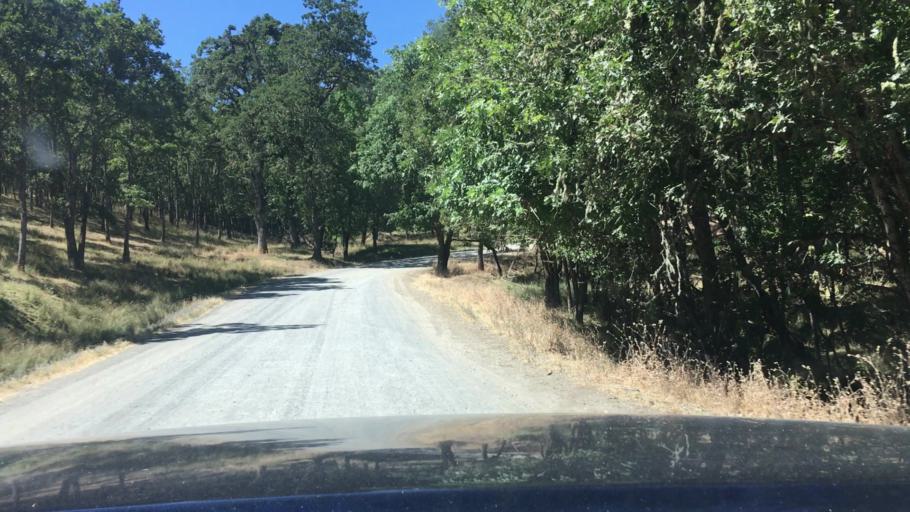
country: US
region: Oregon
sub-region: Douglas County
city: Winston
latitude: 43.1383
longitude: -123.4411
